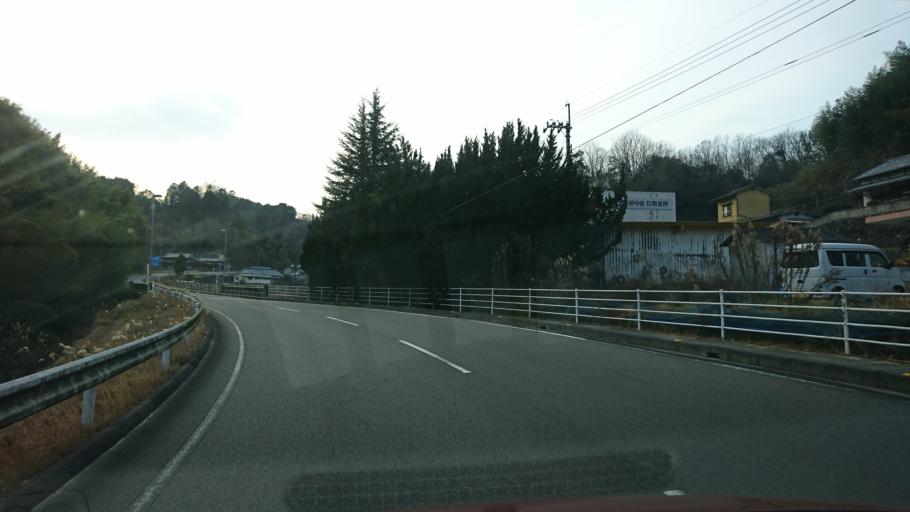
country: JP
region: Ehime
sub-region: Shikoku-chuo Shi
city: Matsuyama
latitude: 33.9031
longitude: 132.8176
